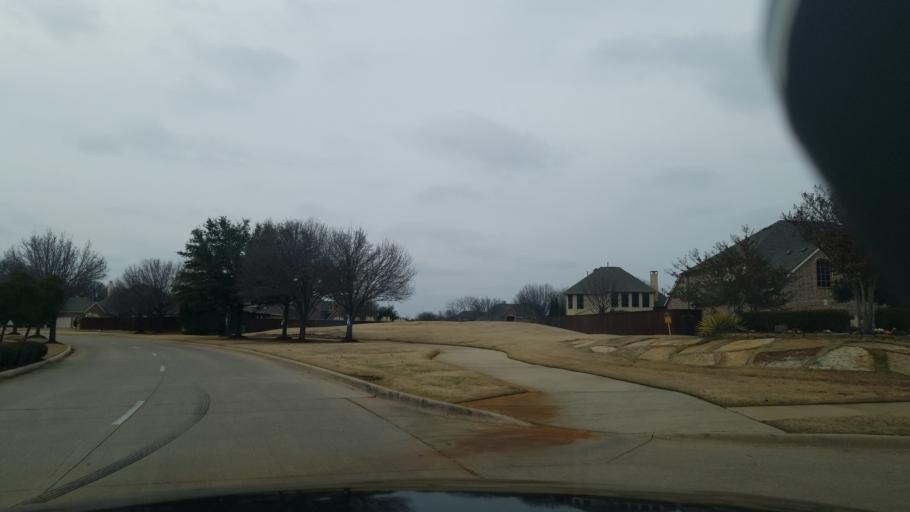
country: US
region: Texas
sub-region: Denton County
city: Shady Shores
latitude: 33.1522
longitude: -97.0427
